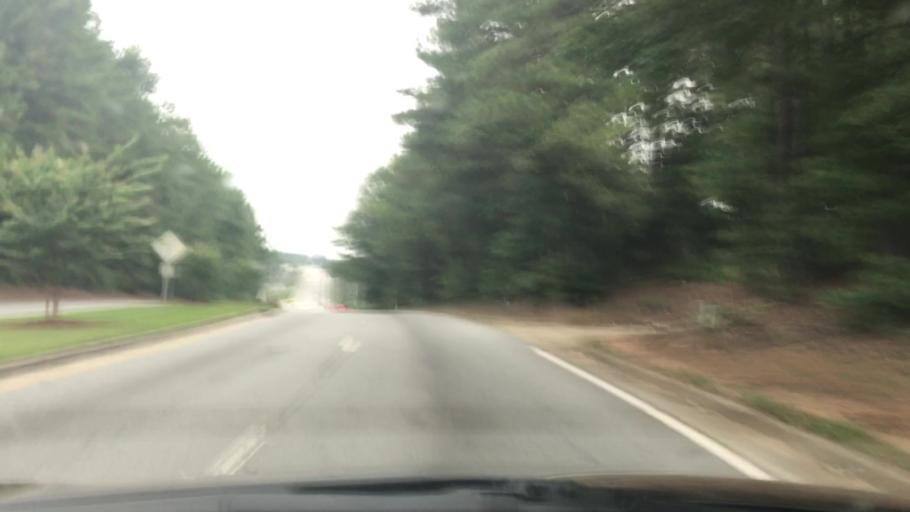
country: US
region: Georgia
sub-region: DeKalb County
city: Tucker
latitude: 33.8604
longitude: -84.1875
